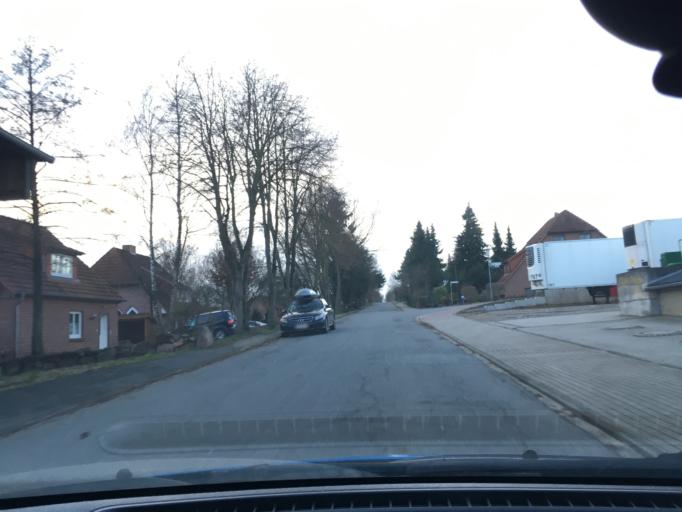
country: DE
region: Lower Saxony
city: Amelinghausen
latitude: 53.1270
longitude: 10.2114
